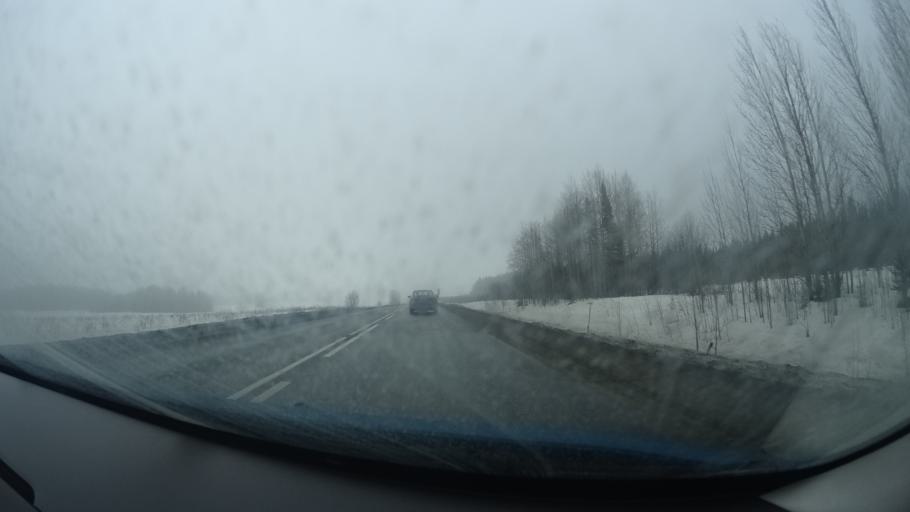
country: RU
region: Perm
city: Kuyeda
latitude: 56.4702
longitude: 55.6968
